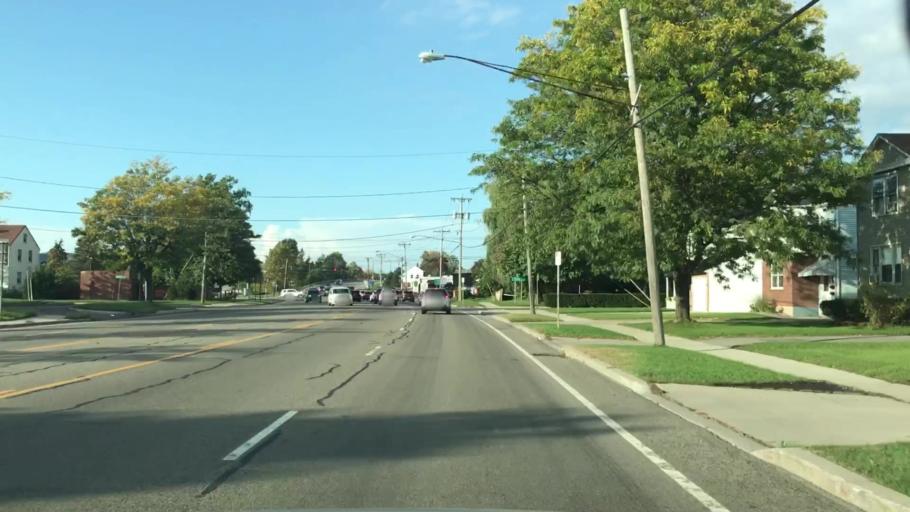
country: US
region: New York
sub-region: Erie County
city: Williamsville
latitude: 42.9480
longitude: -78.7543
